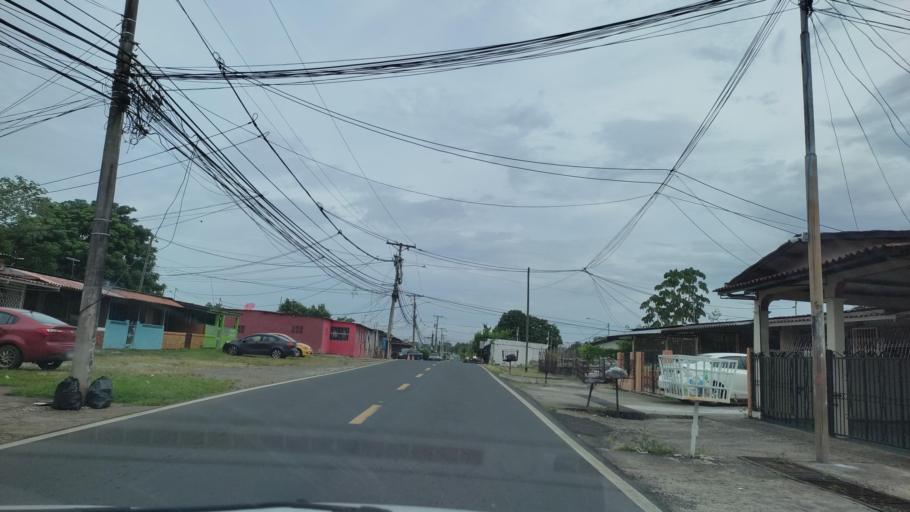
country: PA
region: Panama
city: San Miguelito
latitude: 9.0482
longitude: -79.4312
